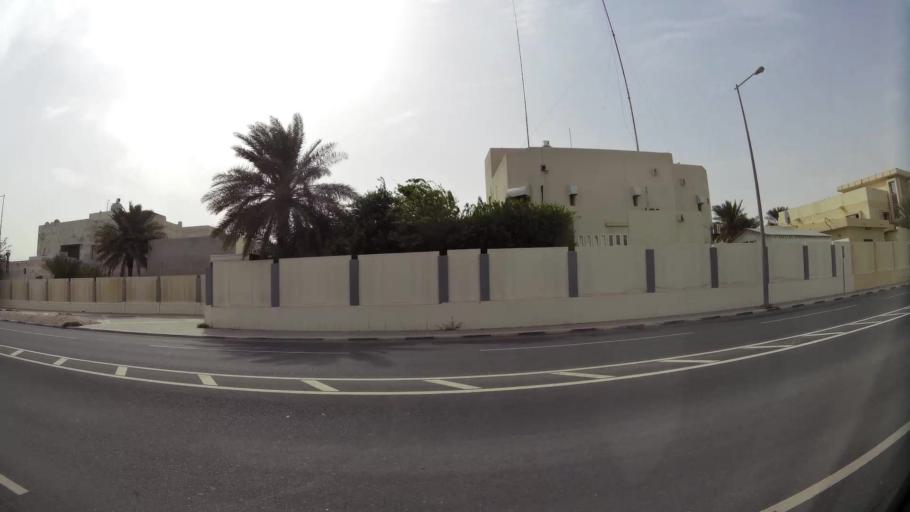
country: QA
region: Baladiyat ad Dawhah
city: Doha
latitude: 25.3227
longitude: 51.5067
